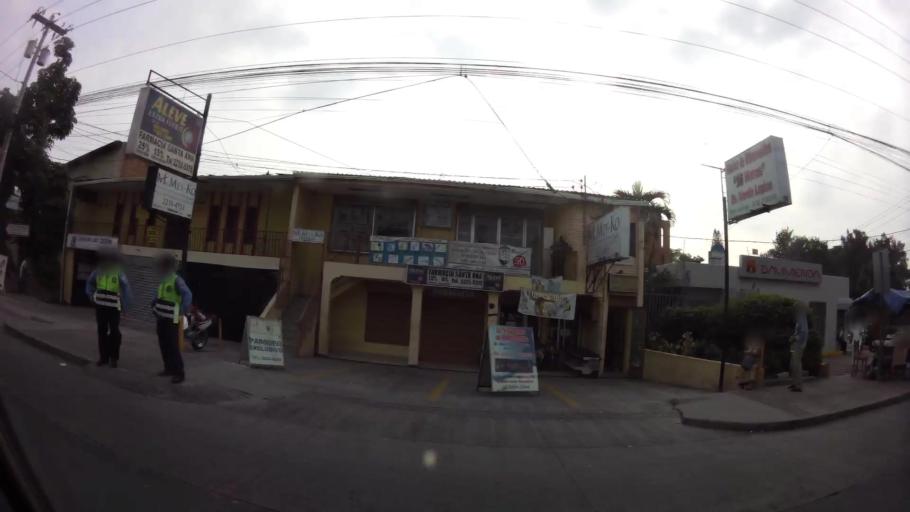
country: HN
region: Francisco Morazan
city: Tegucigalpa
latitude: 14.0905
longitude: -87.1970
